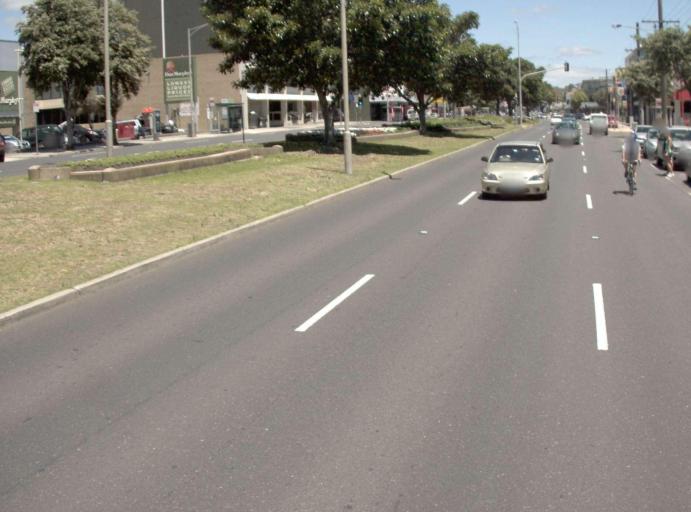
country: AU
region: Victoria
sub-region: Frankston
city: Frankston
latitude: -38.1410
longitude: 145.1219
